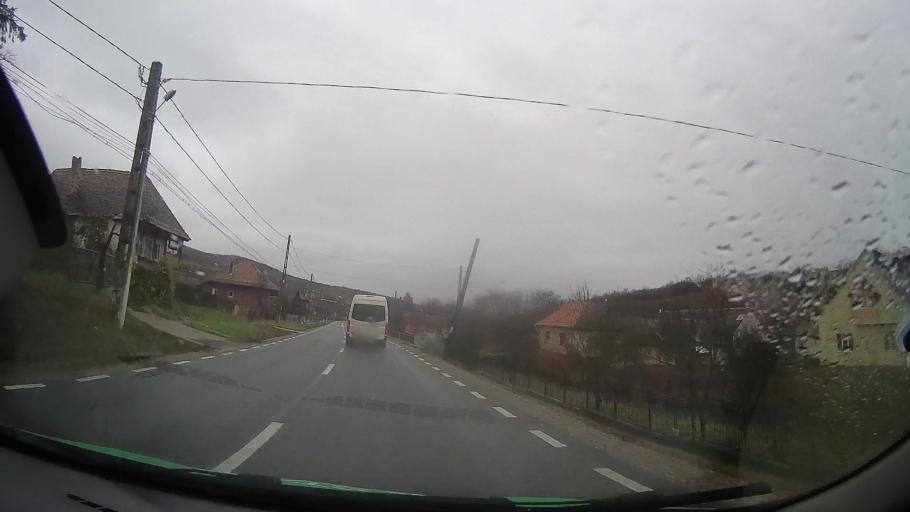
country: RO
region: Bistrita-Nasaud
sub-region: Comuna Galatii Bistritei
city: Galatii Bistritei
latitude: 47.0244
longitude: 24.4154
